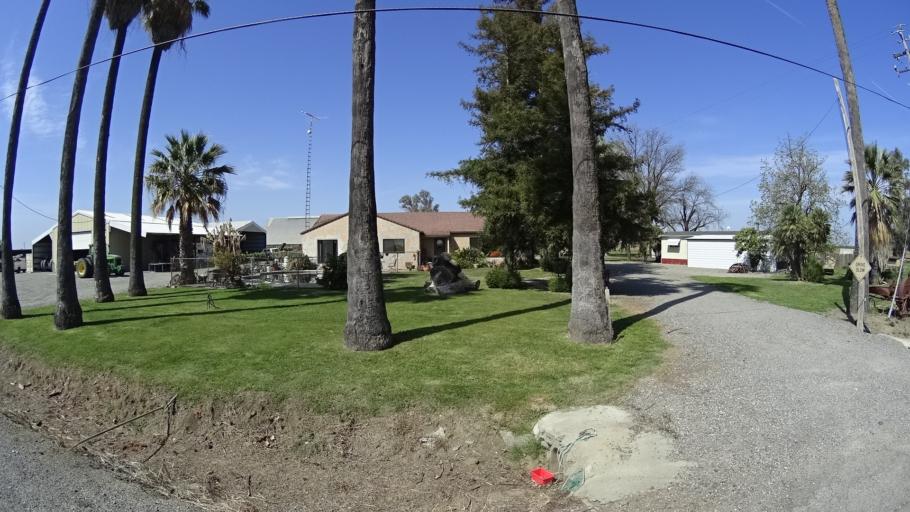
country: US
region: California
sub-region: Glenn County
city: Hamilton City
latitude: 39.6233
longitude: -122.0557
